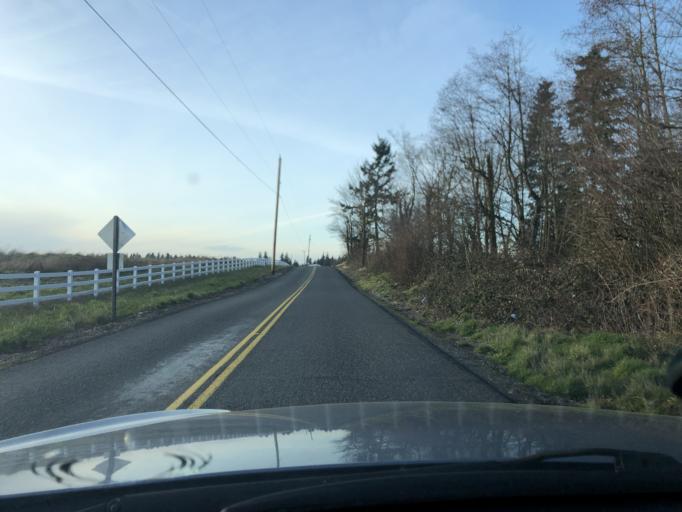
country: US
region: Washington
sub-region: Pierce County
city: Prairie Ridge
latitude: 47.1962
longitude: -122.1136
